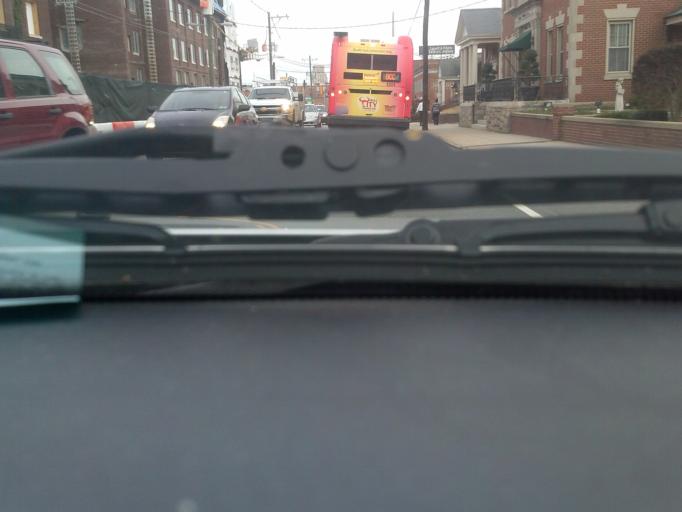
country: US
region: North Carolina
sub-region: Durham County
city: Durham
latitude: 36.0019
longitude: -78.9123
